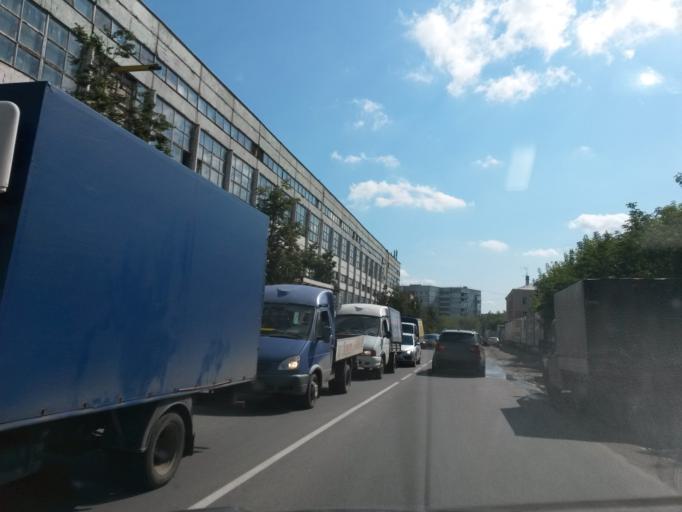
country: RU
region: Ivanovo
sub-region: Gorod Ivanovo
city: Ivanovo
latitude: 57.0098
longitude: 40.9535
